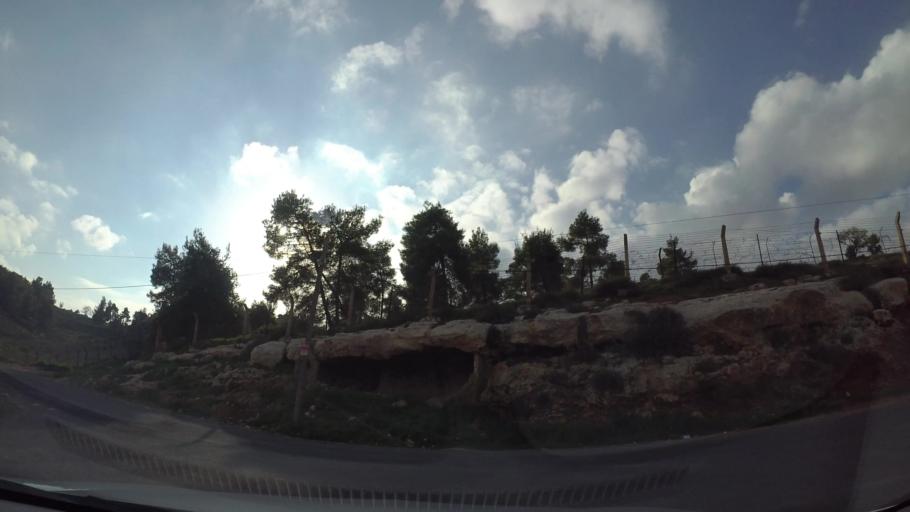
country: JO
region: Amman
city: Al Jubayhah
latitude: 32.0096
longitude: 35.8596
